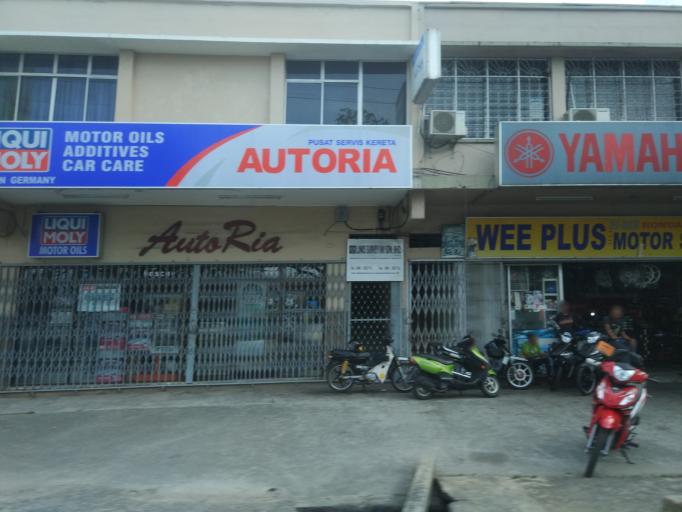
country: MY
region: Sabah
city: Kota Kinabalu
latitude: 5.9929
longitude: 116.1135
